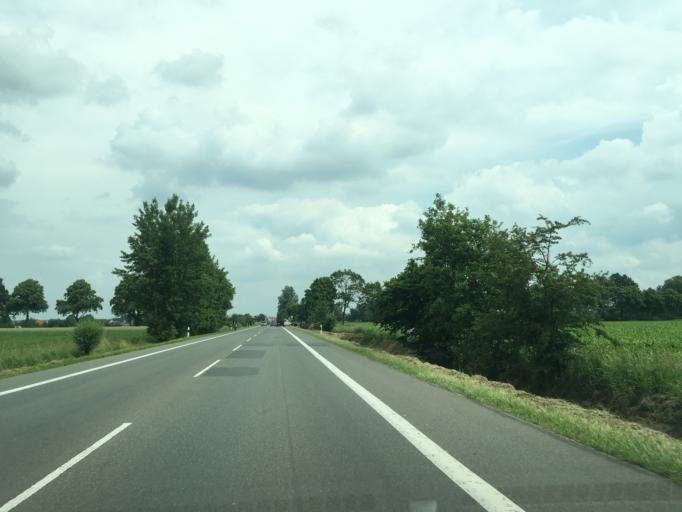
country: DE
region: North Rhine-Westphalia
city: Emsdetten
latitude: 52.1641
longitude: 7.4922
